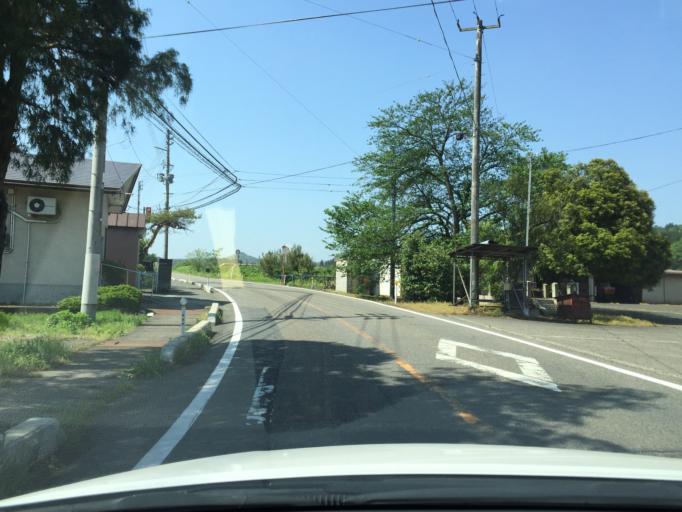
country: JP
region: Niigata
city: Muramatsu
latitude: 37.6822
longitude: 139.1507
